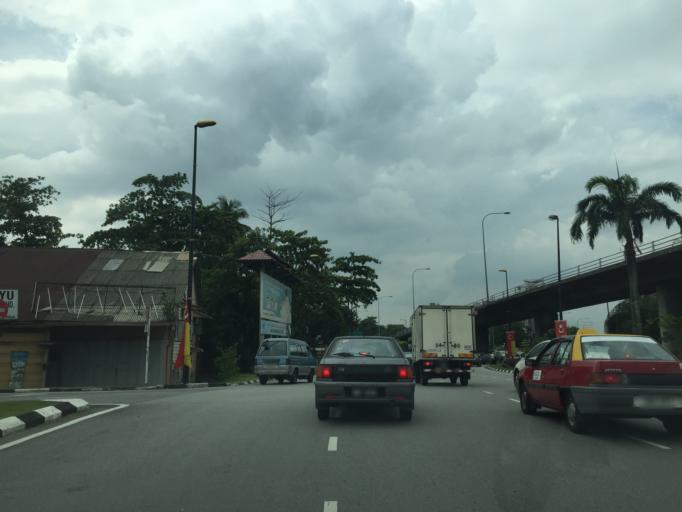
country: MY
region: Selangor
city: Klang
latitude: 3.0365
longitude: 101.4436
